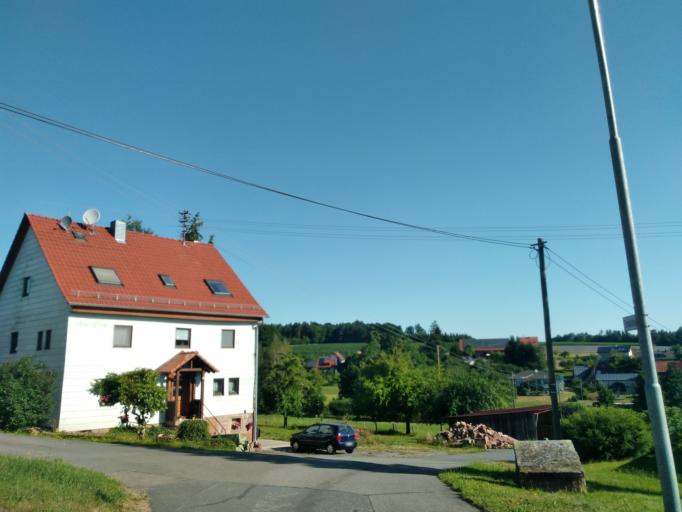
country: DE
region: Baden-Wuerttemberg
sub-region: Karlsruhe Region
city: Mudau
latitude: 49.5155
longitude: 9.1960
